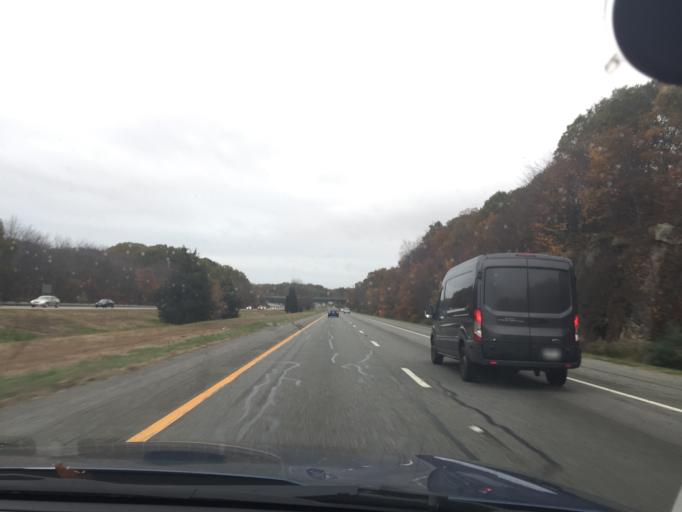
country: US
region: Rhode Island
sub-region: Providence County
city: Johnston
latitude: 41.7846
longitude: -71.5040
